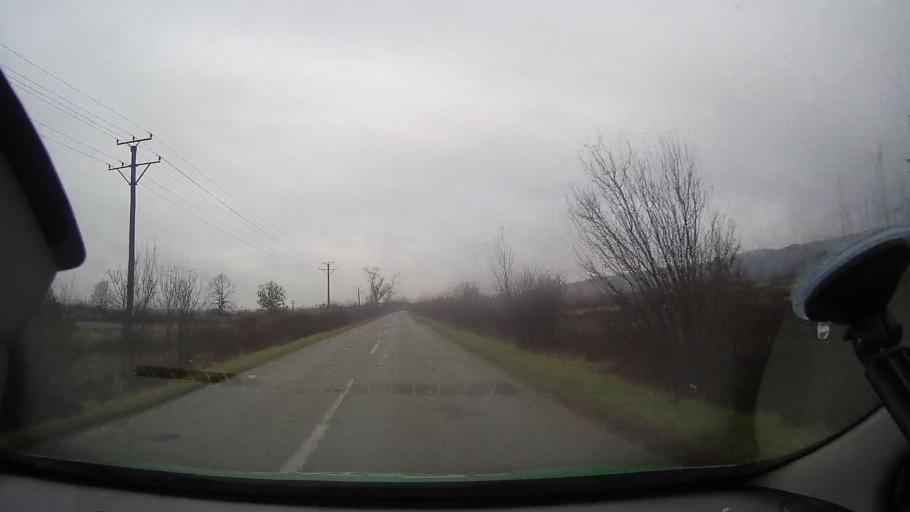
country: RO
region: Arad
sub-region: Comuna Ignesti
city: Ignesti
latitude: 46.4049
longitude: 22.2054
